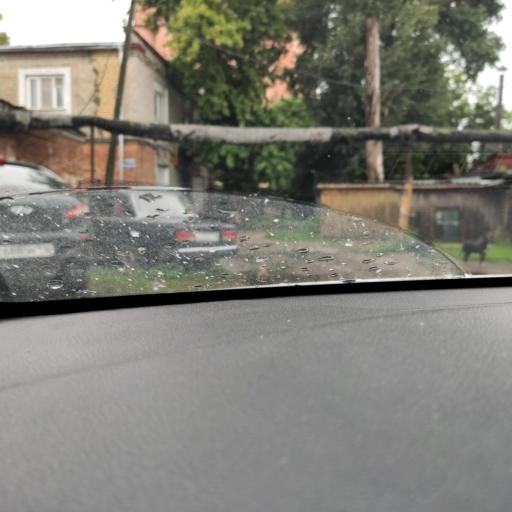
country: RU
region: Tatarstan
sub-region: Gorod Kazan'
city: Kazan
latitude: 55.7613
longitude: 49.0796
